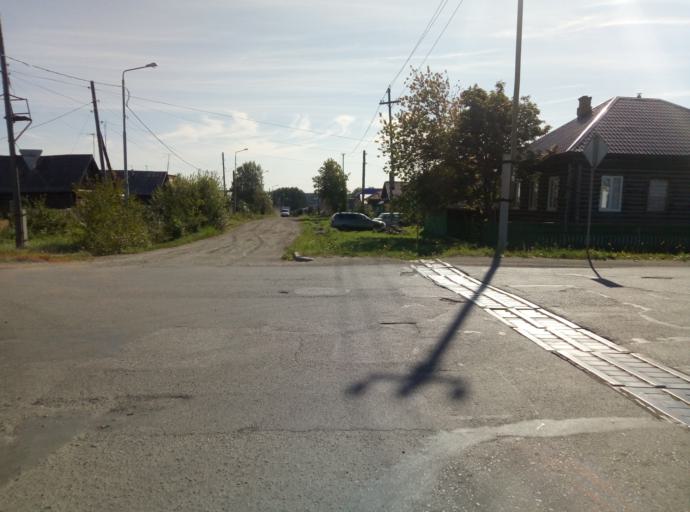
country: RU
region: Sverdlovsk
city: Karpinsk
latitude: 59.7618
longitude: 60.0165
